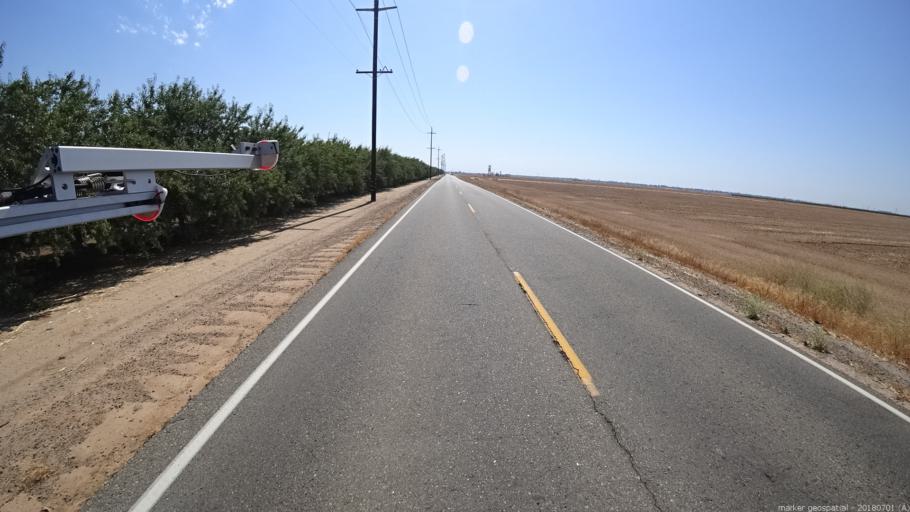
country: US
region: California
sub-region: Madera County
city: Bonadelle Ranchos-Madera Ranchos
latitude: 36.8802
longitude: -119.8290
